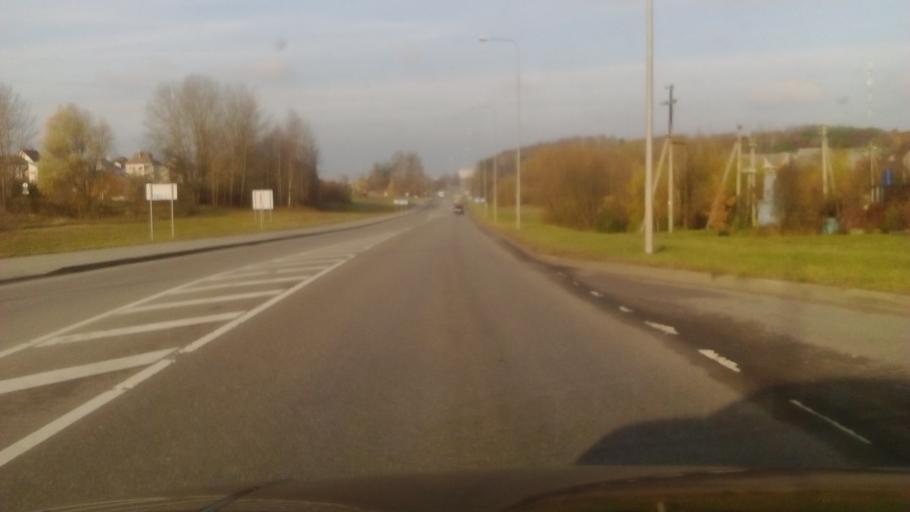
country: LT
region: Alytaus apskritis
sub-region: Alytus
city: Alytus
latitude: 54.3975
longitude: 23.9998
